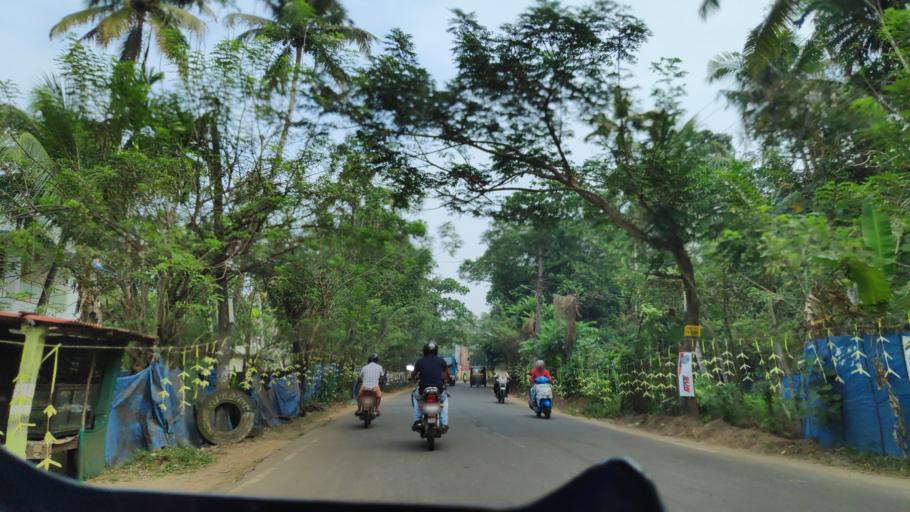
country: IN
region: Kerala
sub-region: Alappuzha
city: Shertallai
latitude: 9.7099
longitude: 76.3577
